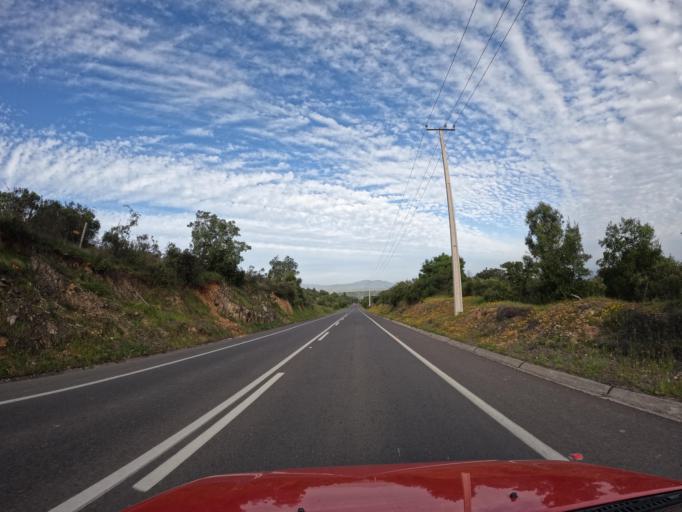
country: CL
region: Valparaiso
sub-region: San Antonio Province
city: San Antonio
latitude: -34.0496
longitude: -71.6145
